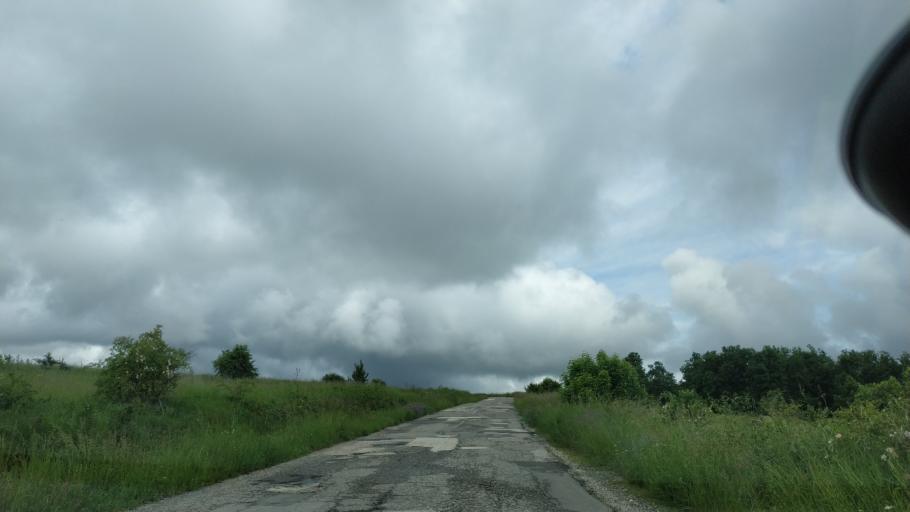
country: RS
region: Central Serbia
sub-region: Zajecarski Okrug
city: Soko Banja
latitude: 43.6970
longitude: 21.9387
